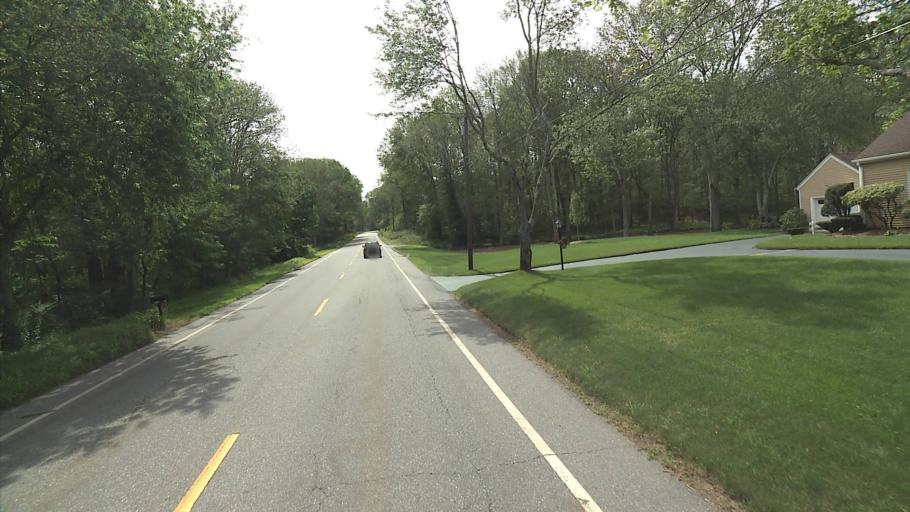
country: US
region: Connecticut
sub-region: Windham County
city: Putnam
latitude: 41.9101
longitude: -71.8689
